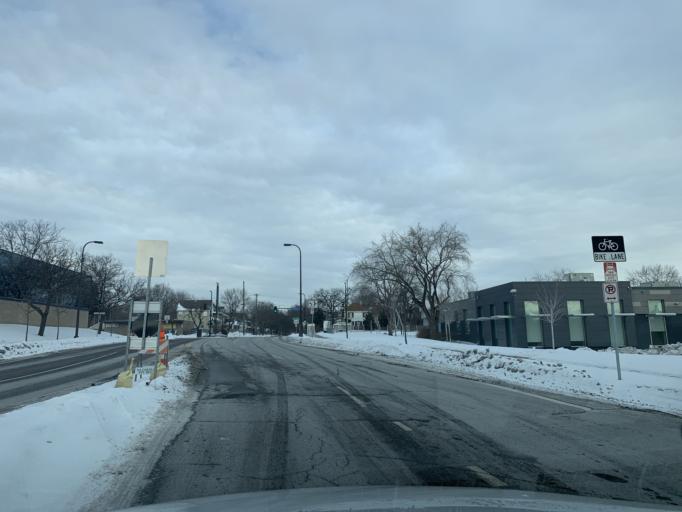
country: US
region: Minnesota
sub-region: Hennepin County
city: Minneapolis
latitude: 44.9911
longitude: -93.2940
